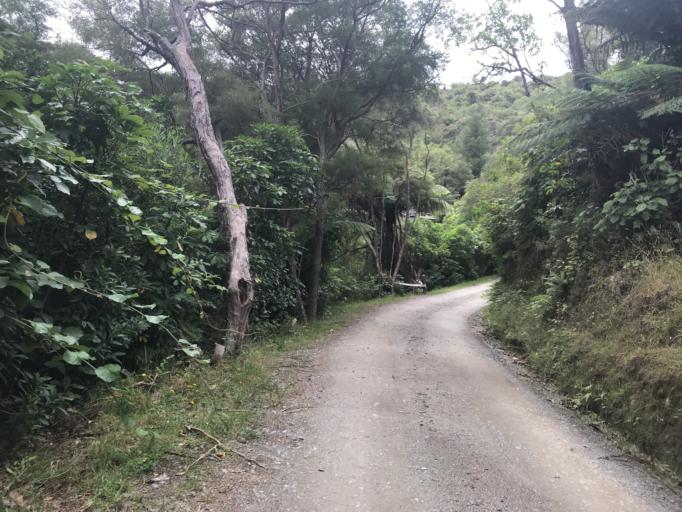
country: NZ
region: Marlborough
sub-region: Marlborough District
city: Picton
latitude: -41.2217
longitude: 173.9724
